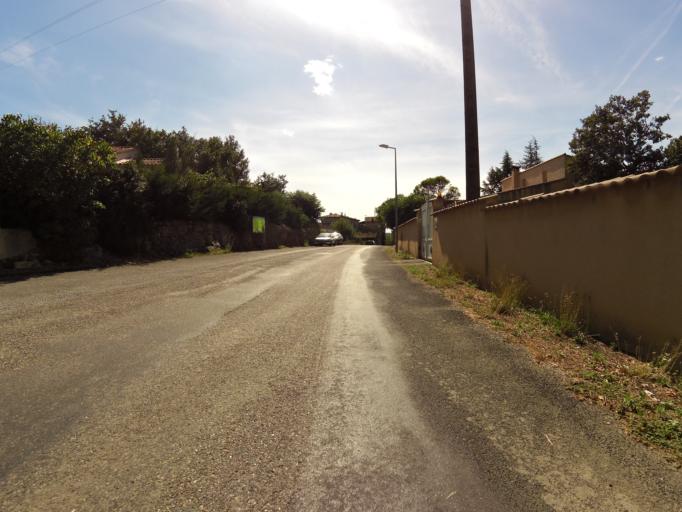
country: FR
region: Languedoc-Roussillon
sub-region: Departement du Gard
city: Quissac
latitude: 43.9562
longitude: 4.0337
